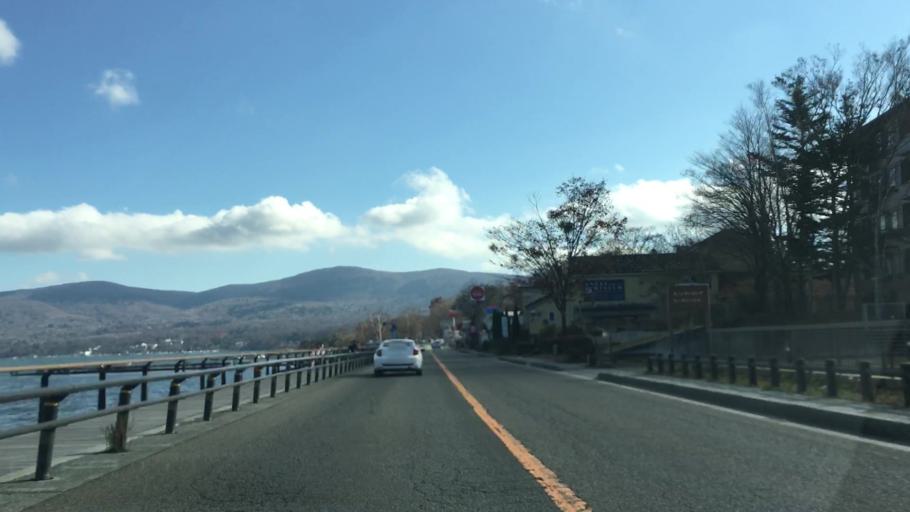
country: JP
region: Shizuoka
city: Gotemba
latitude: 35.4190
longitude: 138.8549
